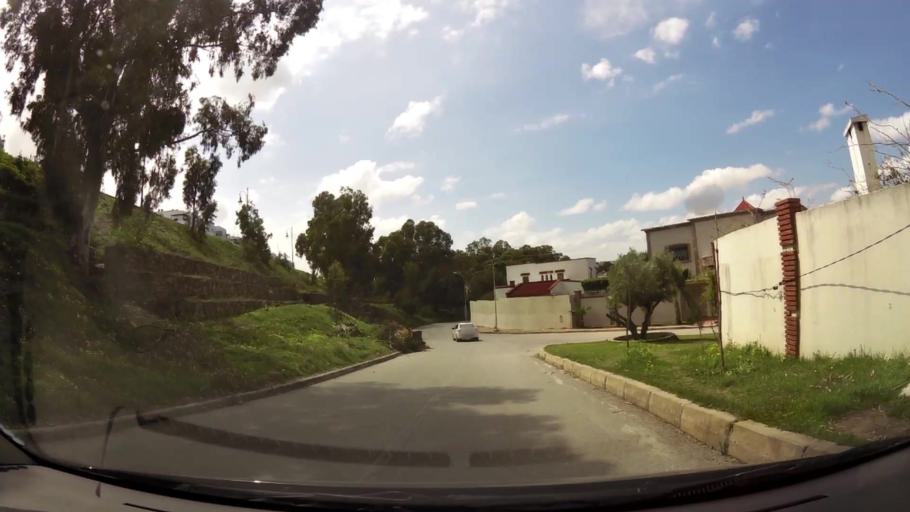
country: MA
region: Tanger-Tetouan
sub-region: Tanger-Assilah
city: Tangier
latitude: 35.7823
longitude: -5.7603
